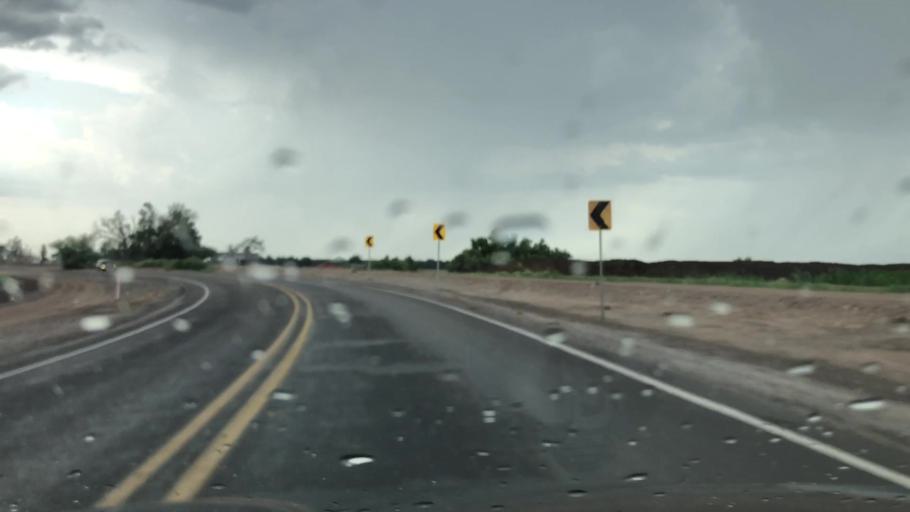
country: US
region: New Mexico
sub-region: Dona Ana County
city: Vado
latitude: 32.0677
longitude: -106.6797
